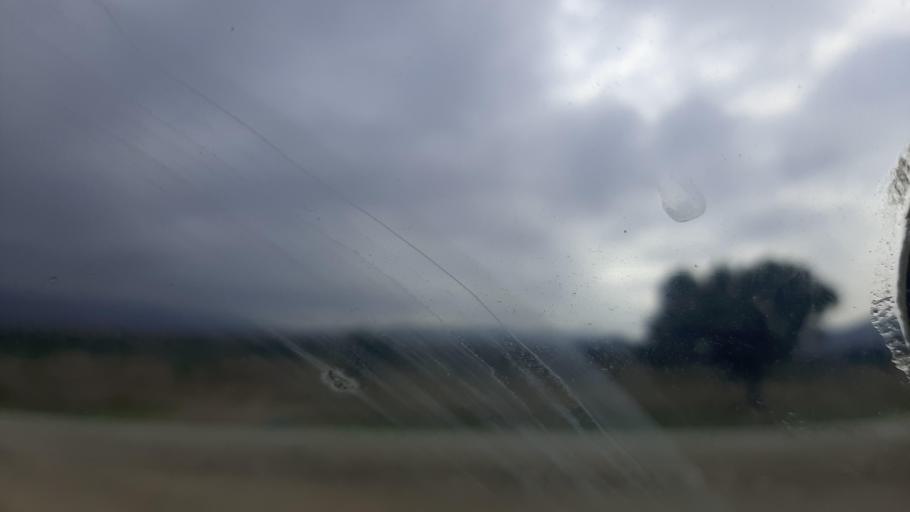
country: TN
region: Tunis
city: La Sebala du Mornag
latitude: 36.5641
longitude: 10.2934
